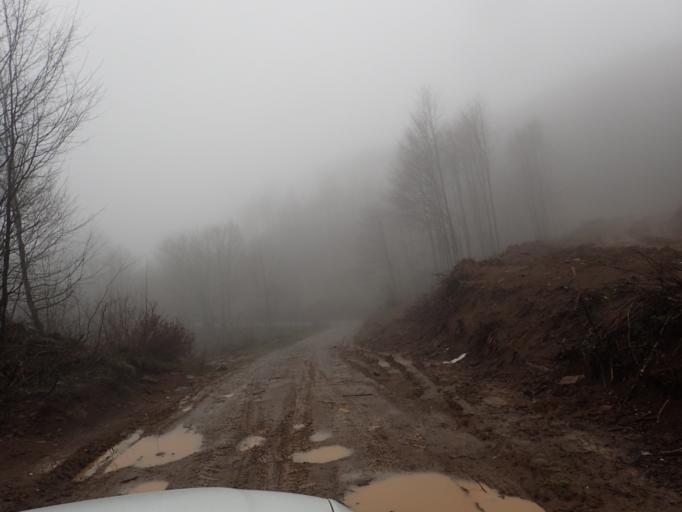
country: TR
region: Ordu
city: Kumru
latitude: 40.7949
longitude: 37.2663
